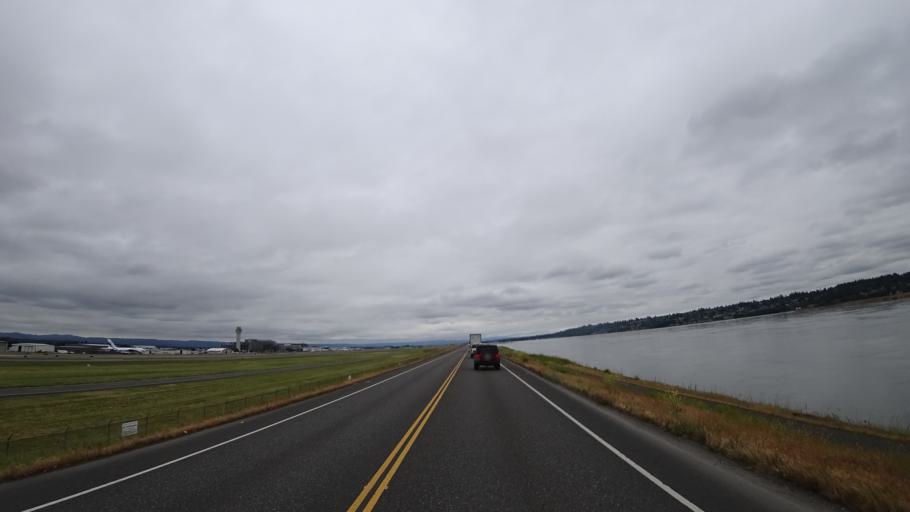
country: US
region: Washington
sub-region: Clark County
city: Orchards
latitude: 45.5886
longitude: -122.5734
